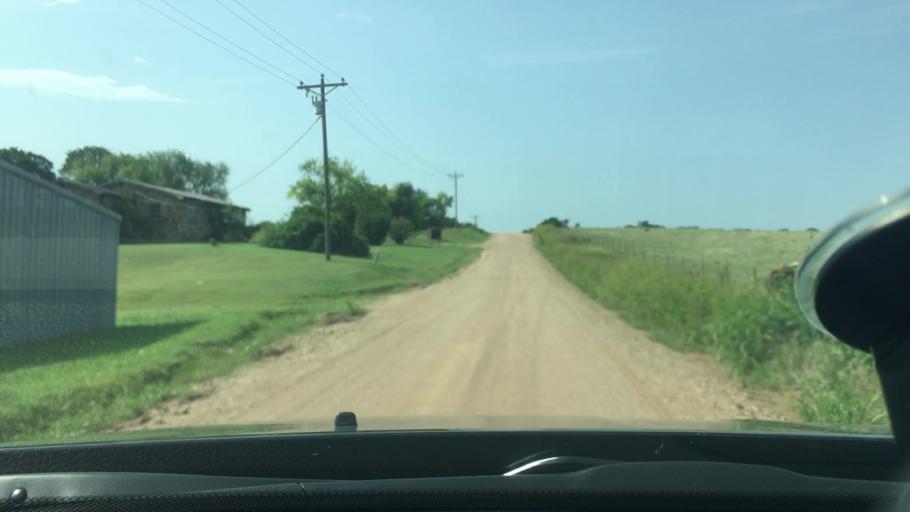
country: US
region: Oklahoma
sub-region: Atoka County
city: Atoka
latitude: 34.4600
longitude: -96.0407
